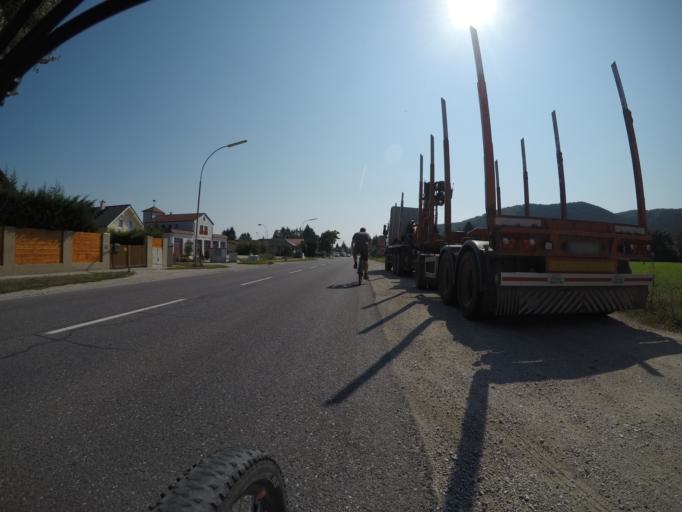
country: AT
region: Lower Austria
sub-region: Politischer Bezirk Baden
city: Hirtenberg
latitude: 47.9374
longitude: 16.1479
